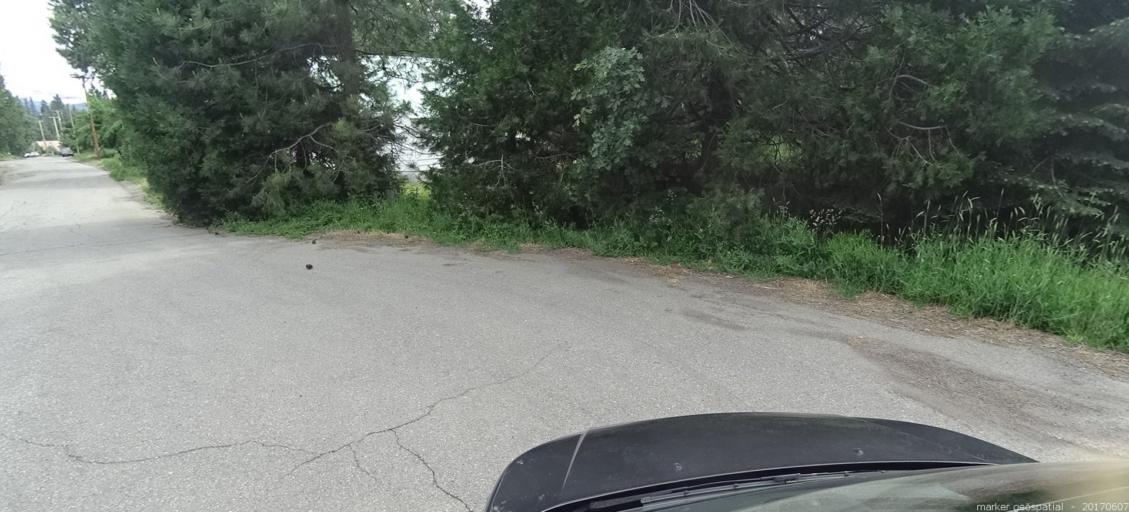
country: US
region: California
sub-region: Siskiyou County
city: McCloud
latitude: 41.2493
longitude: -122.1412
